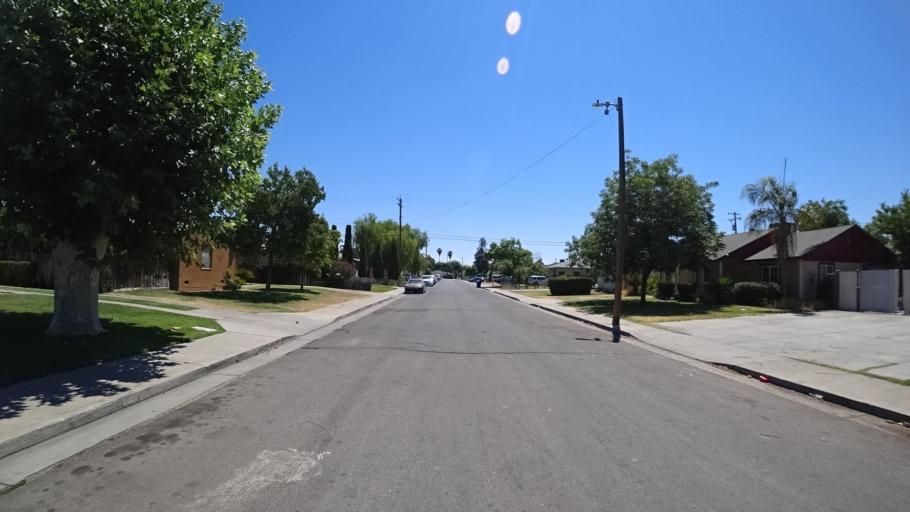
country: US
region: California
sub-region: Fresno County
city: Fresno
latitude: 36.7401
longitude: -119.7406
